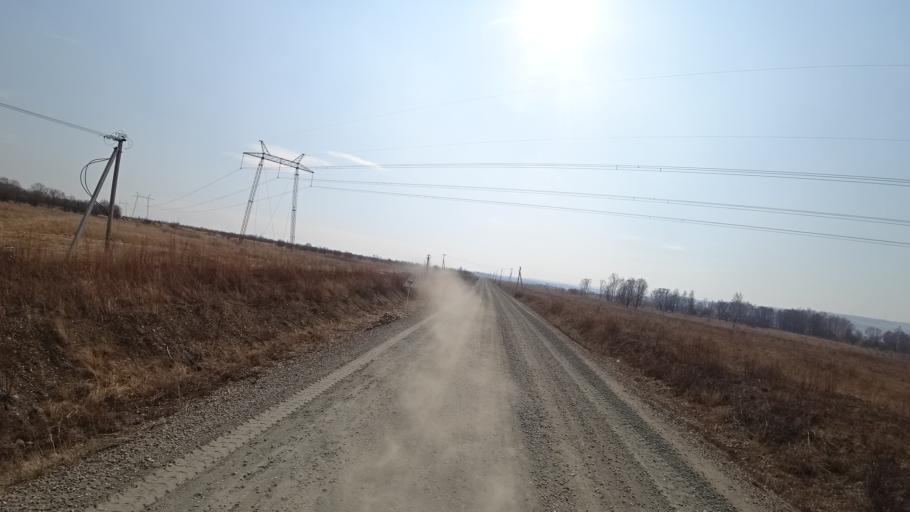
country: RU
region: Amur
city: Novobureyskiy
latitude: 49.8153
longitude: 129.9753
